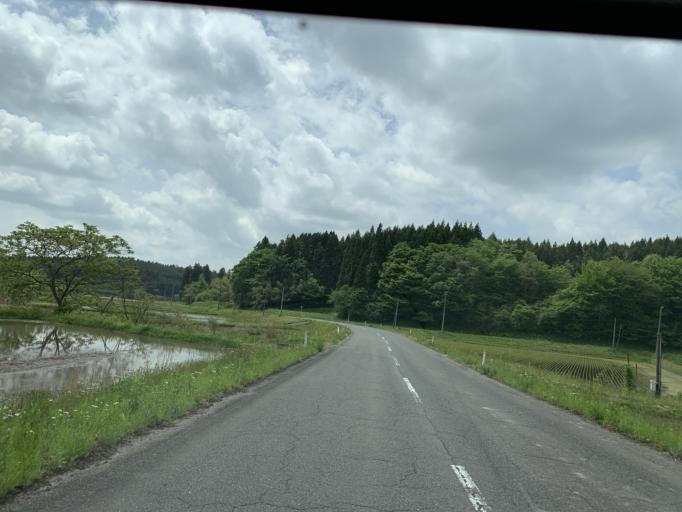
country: JP
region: Miyagi
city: Furukawa
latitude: 38.7074
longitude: 140.9182
